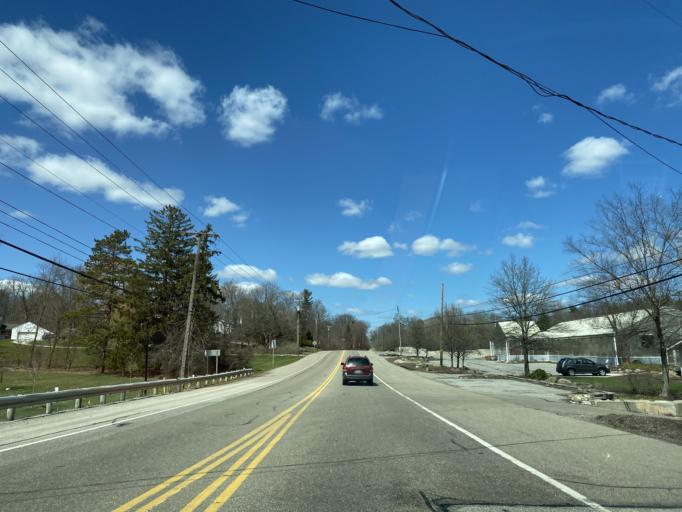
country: US
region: Ohio
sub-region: Summit County
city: Montrose-Ghent
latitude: 41.1700
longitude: -81.6368
